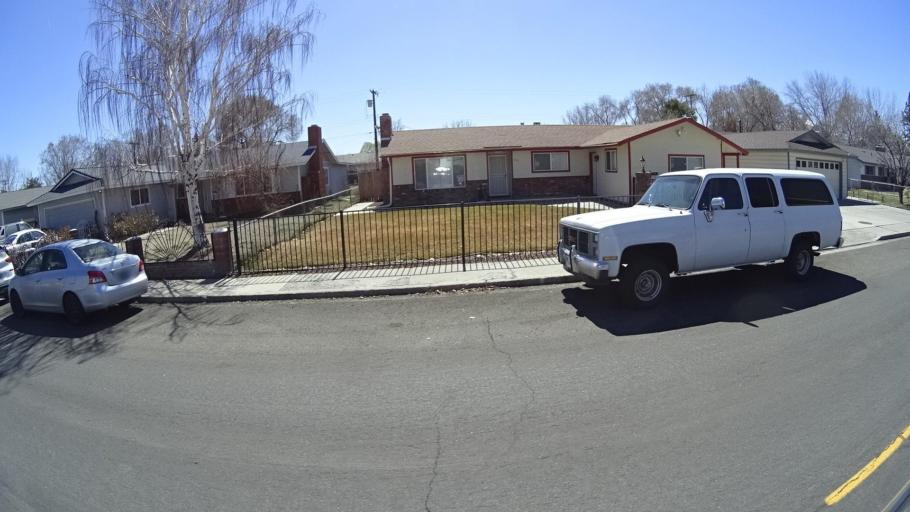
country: US
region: Nevada
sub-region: Washoe County
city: Sparks
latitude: 39.5528
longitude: -119.7459
